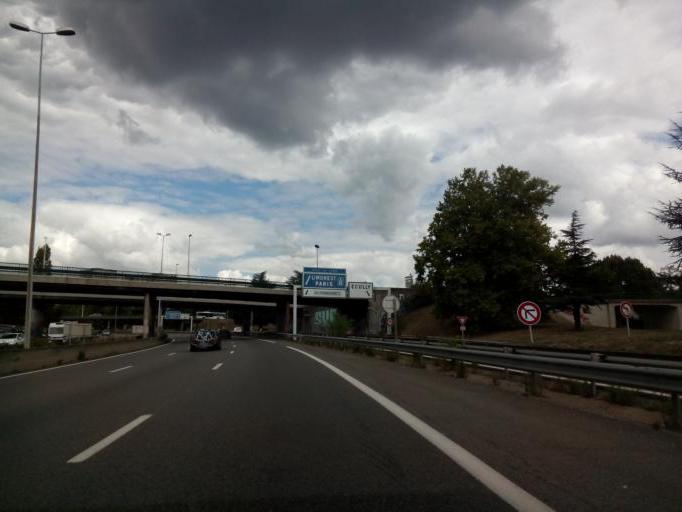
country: FR
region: Rhone-Alpes
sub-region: Departement du Rhone
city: Ecully
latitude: 45.7846
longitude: 4.7846
